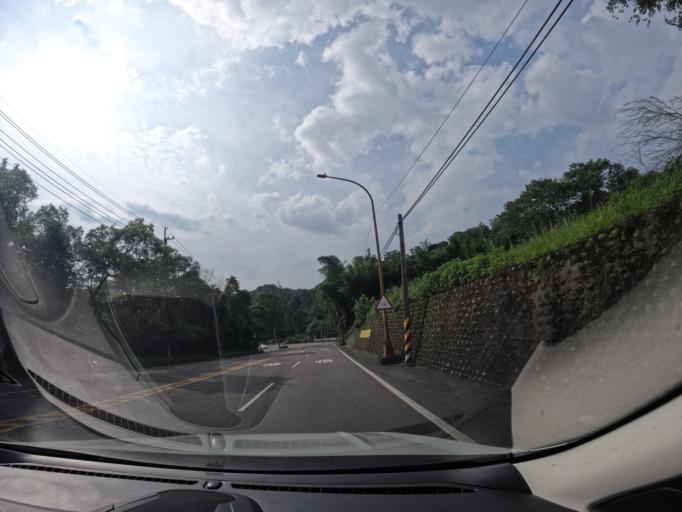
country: TW
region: Taiwan
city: Daxi
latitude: 24.8949
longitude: 121.3235
